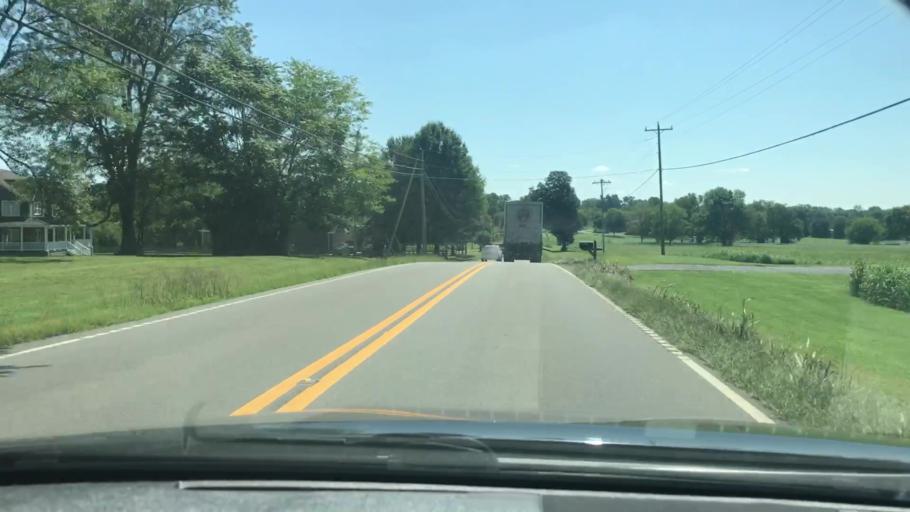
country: US
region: Tennessee
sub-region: Sumner County
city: Gallatin
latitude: 36.4171
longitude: -86.5119
